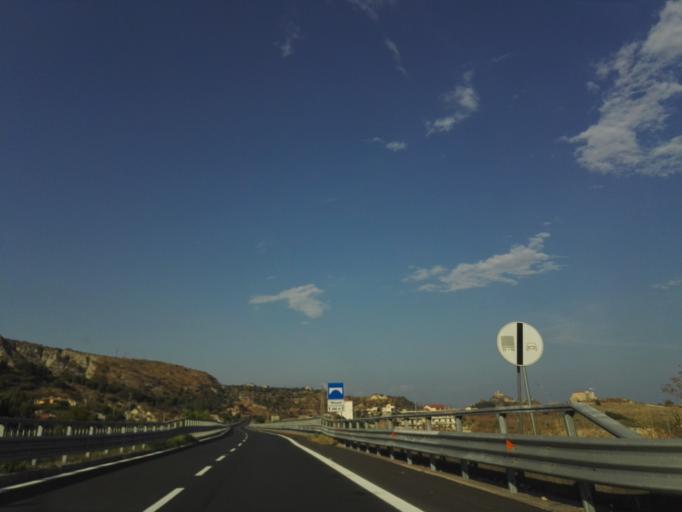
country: IT
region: Calabria
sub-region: Provincia di Reggio Calabria
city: Roccella Ionica
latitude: 38.3250
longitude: 16.3906
